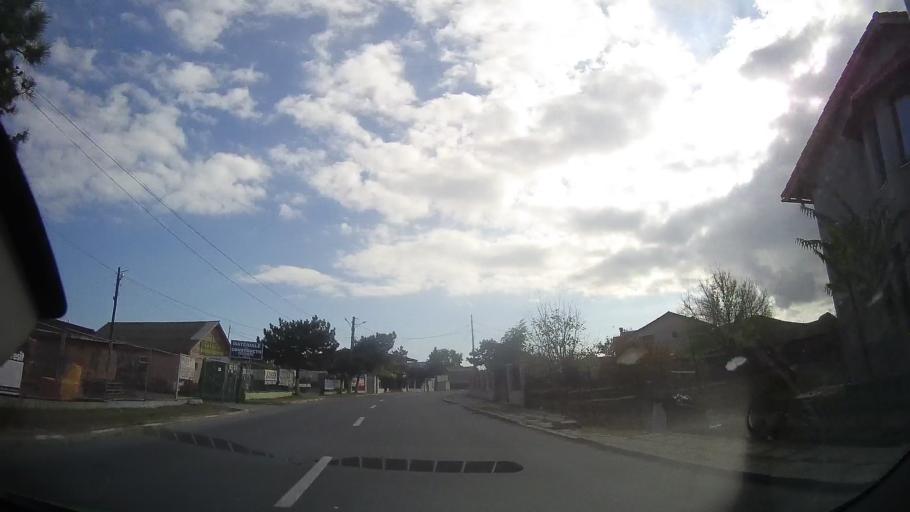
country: RO
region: Constanta
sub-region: Oras Techirghiol
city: Techirghiol
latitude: 44.0622
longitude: 28.5982
